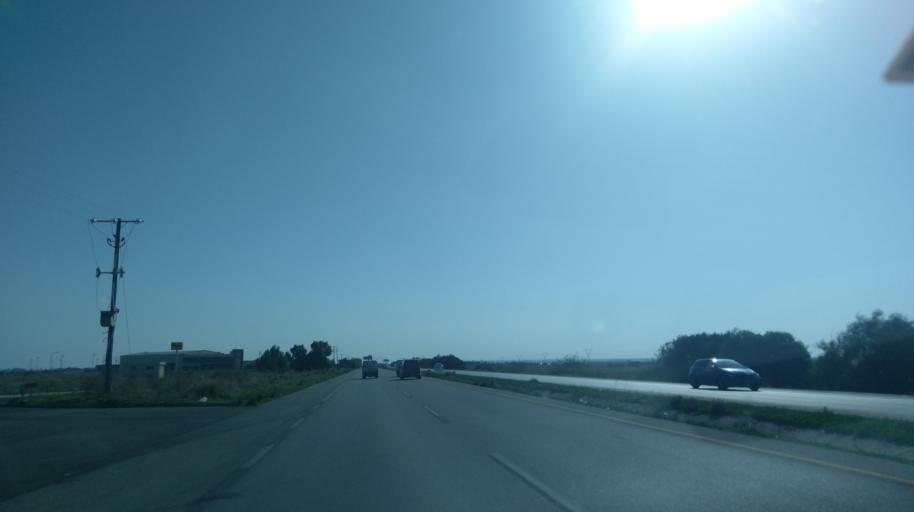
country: CY
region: Ammochostos
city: Acheritou
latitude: 35.1577
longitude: 33.8385
